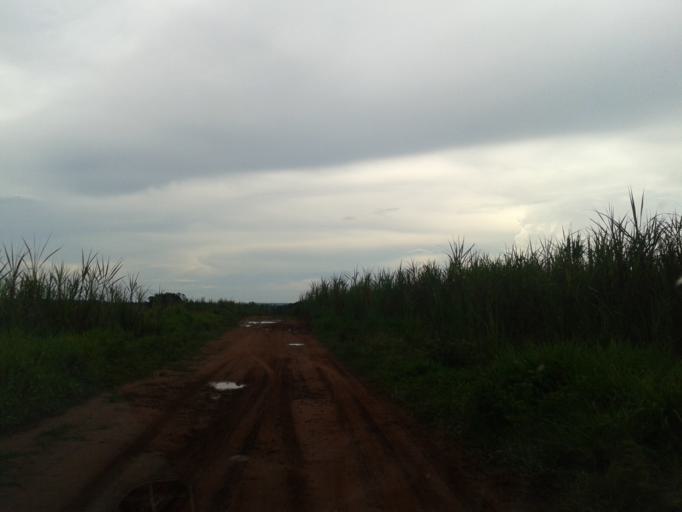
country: BR
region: Minas Gerais
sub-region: Santa Vitoria
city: Santa Vitoria
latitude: -19.1660
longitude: -50.5477
